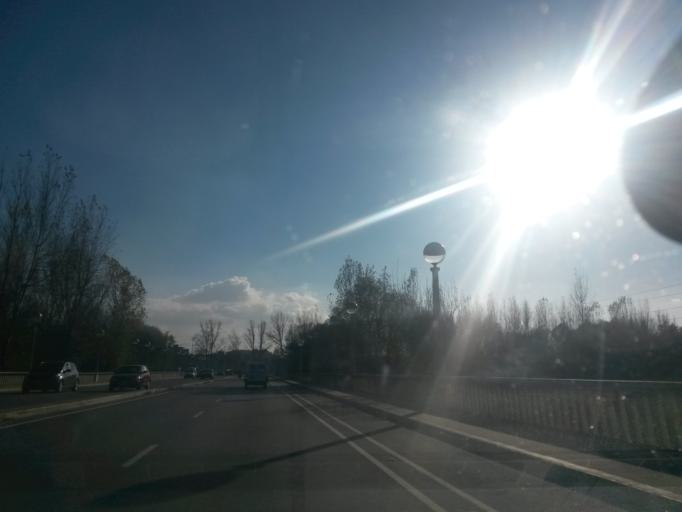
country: ES
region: Catalonia
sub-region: Provincia de Girona
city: Girona
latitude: 41.9868
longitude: 2.8095
